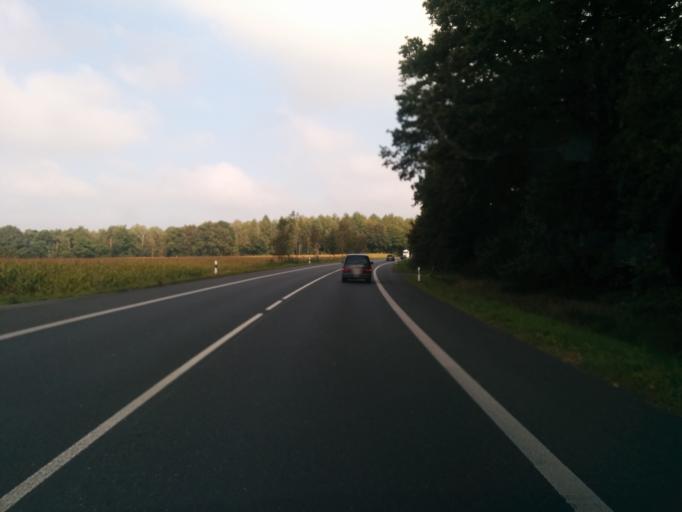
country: DE
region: North Rhine-Westphalia
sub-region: Regierungsbezirk Munster
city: Dulmen
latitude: 51.8718
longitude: 7.2223
